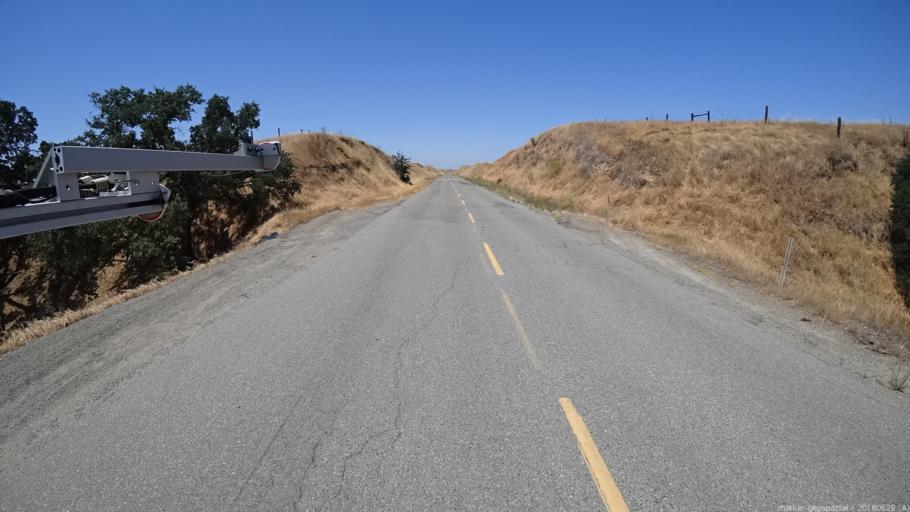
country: US
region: California
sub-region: Madera County
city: Bonadelle Ranchos-Madera Ranchos
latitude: 37.0444
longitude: -119.9239
